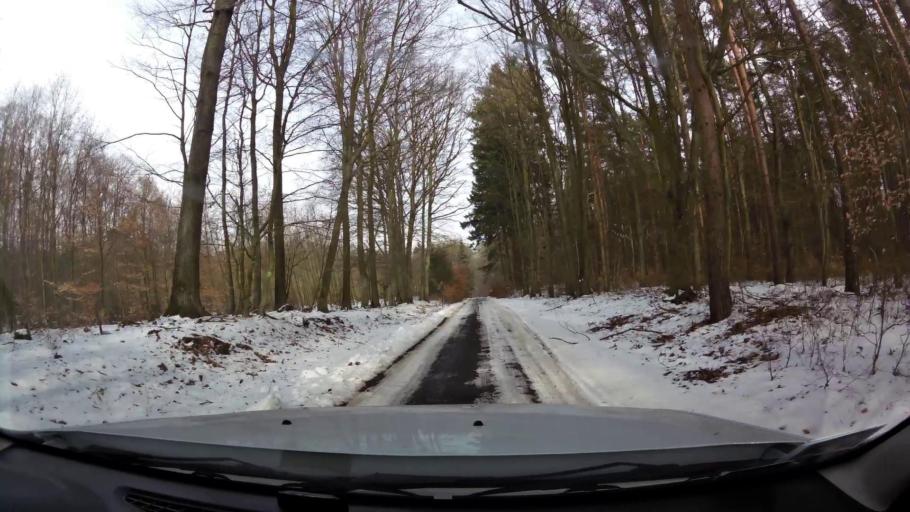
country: PL
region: West Pomeranian Voivodeship
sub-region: Powiat kamienski
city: Miedzyzdroje
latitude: 53.8843
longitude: 14.4867
